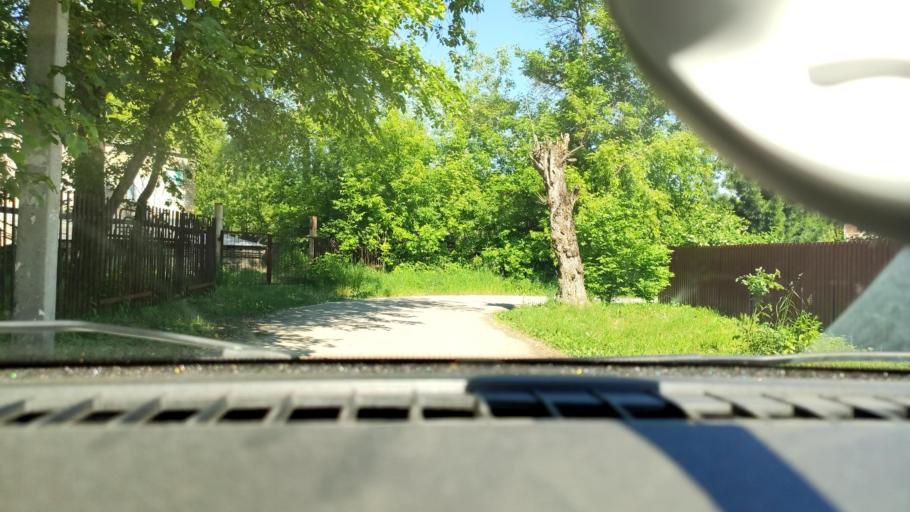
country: RU
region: Perm
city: Perm
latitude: 58.1109
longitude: 56.3132
